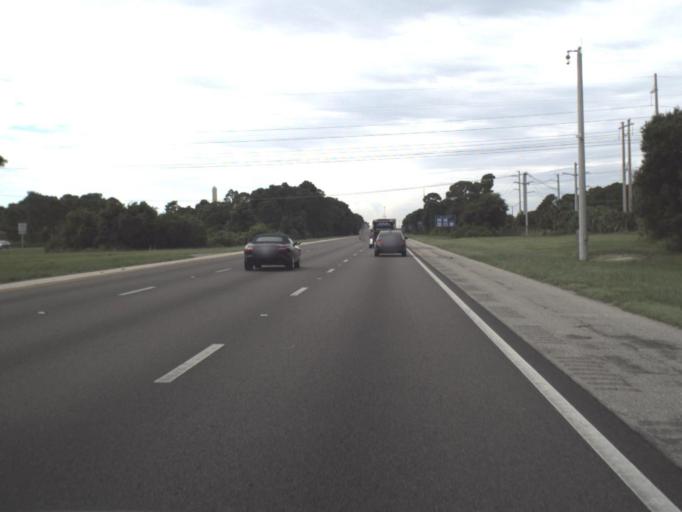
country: US
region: Florida
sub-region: Sarasota County
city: The Meadows
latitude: 27.3585
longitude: -82.4468
